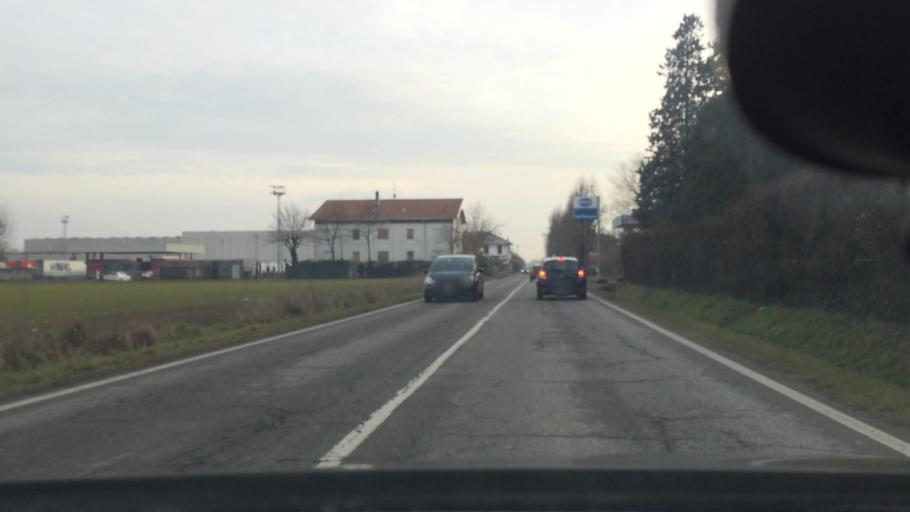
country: IT
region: Lombardy
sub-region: Provincia di Varese
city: Origgio
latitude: 45.5968
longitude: 9.0229
